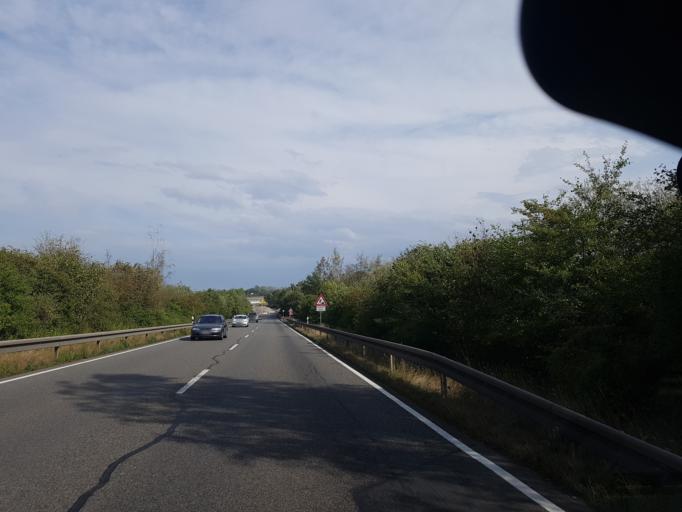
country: DE
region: Saxony
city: Grossweitzschen
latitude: 51.1283
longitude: 13.0454
